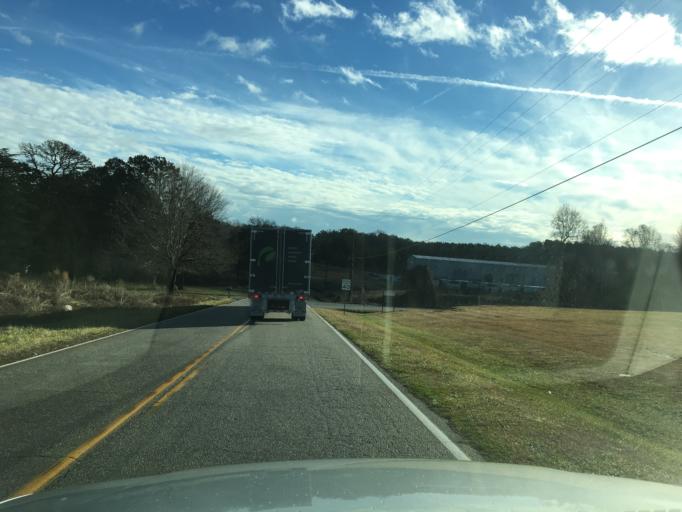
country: US
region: South Carolina
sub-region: Spartanburg County
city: Mayo
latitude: 35.0185
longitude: -81.8828
